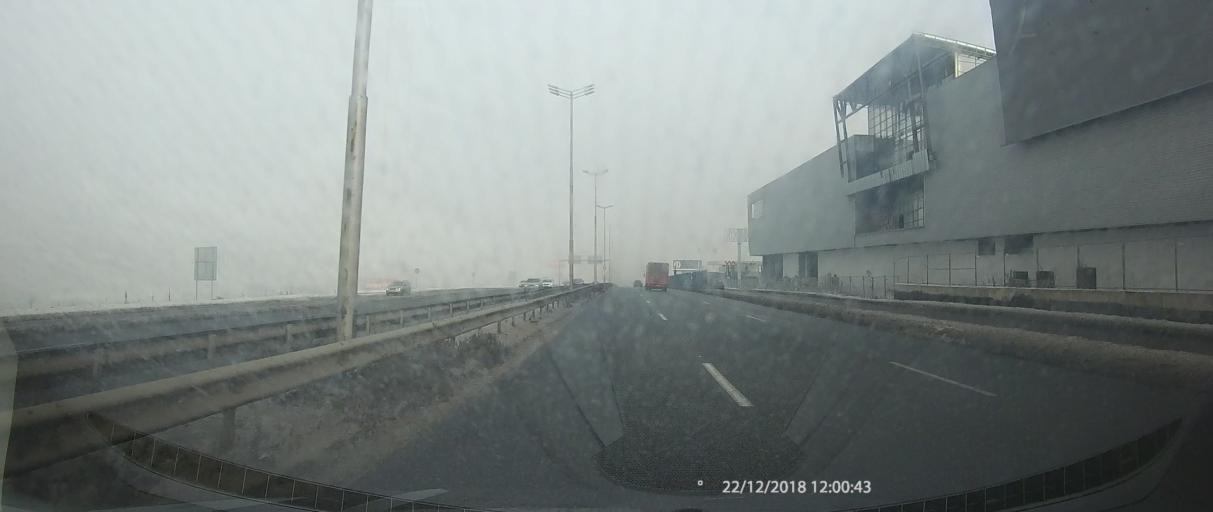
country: BG
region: Sofiya
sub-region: Obshtina Bozhurishte
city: Bozhurishte
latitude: 42.7203
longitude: 23.2365
